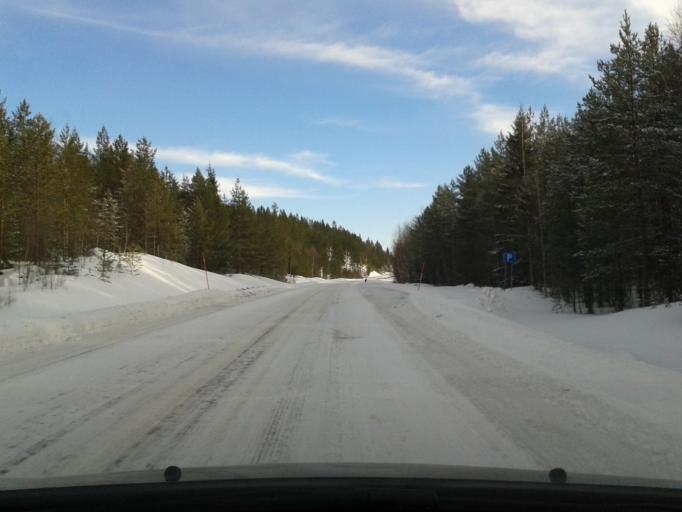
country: SE
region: Vaesterbotten
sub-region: Asele Kommun
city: Asele
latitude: 64.3204
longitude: 17.1145
